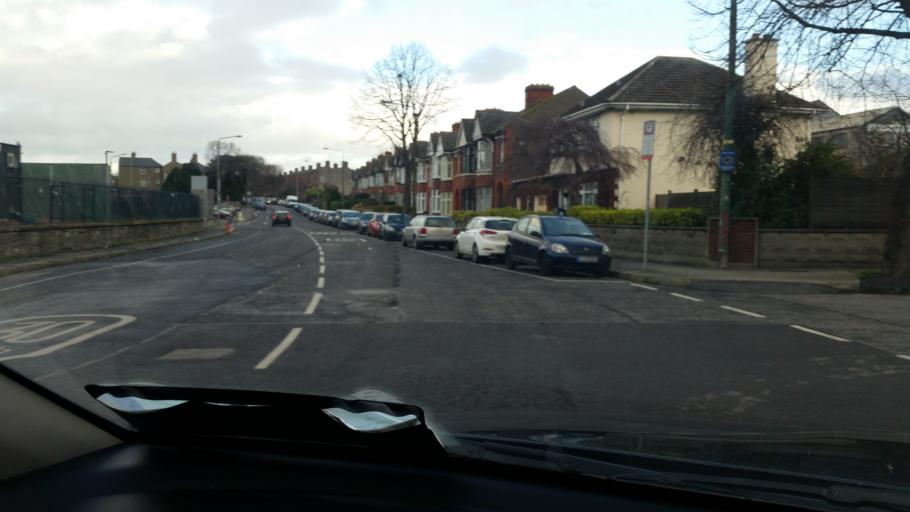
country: IE
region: Leinster
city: Cabra
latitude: 53.3557
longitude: -6.2781
